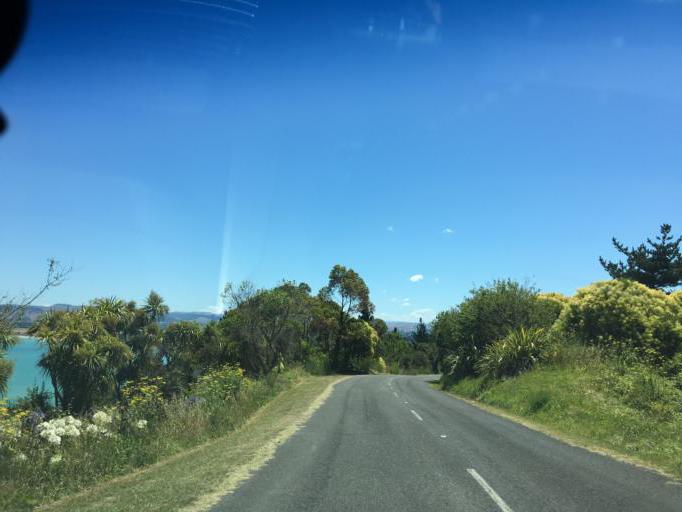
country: NZ
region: Gisborne
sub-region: Gisborne District
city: Gisborne
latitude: -38.6775
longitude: 178.0305
